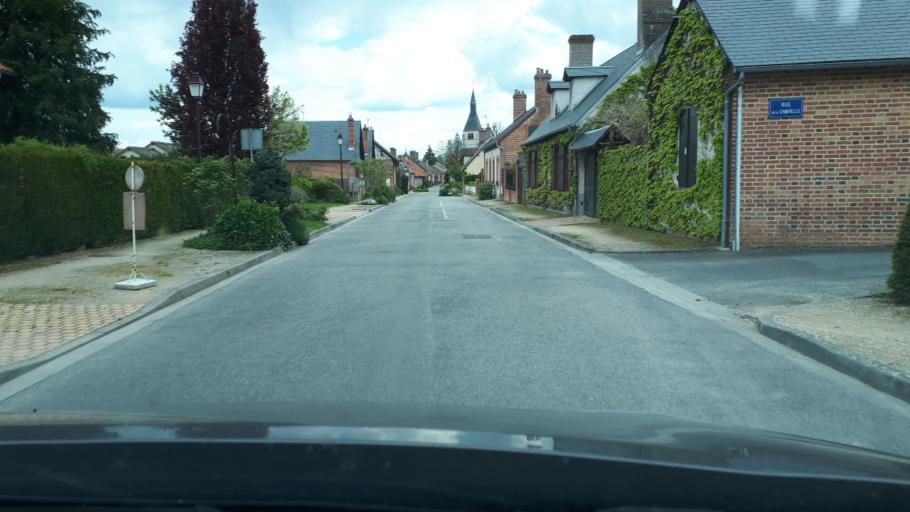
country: FR
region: Centre
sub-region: Departement du Loir-et-Cher
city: Souesmes
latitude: 47.5151
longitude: 2.1479
